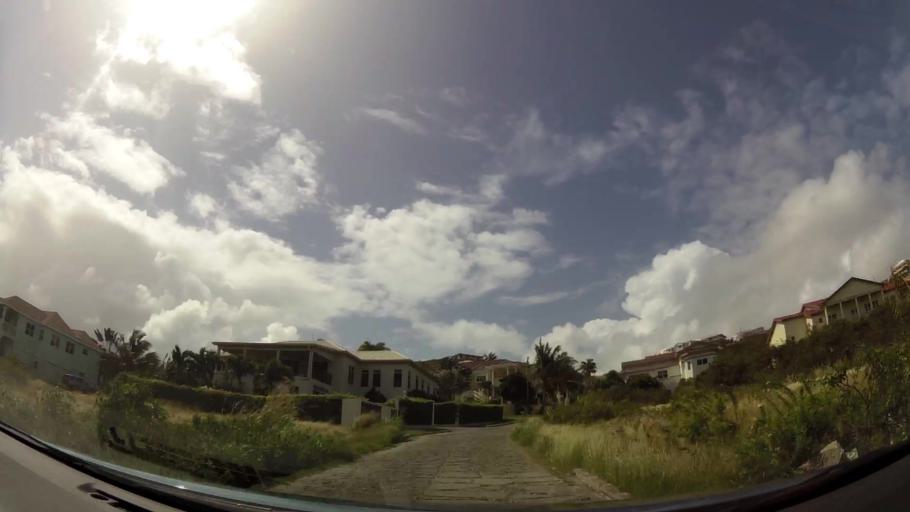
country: KN
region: Saint Peter Basseterre
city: Monkey Hill
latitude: 17.2986
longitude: -62.6924
